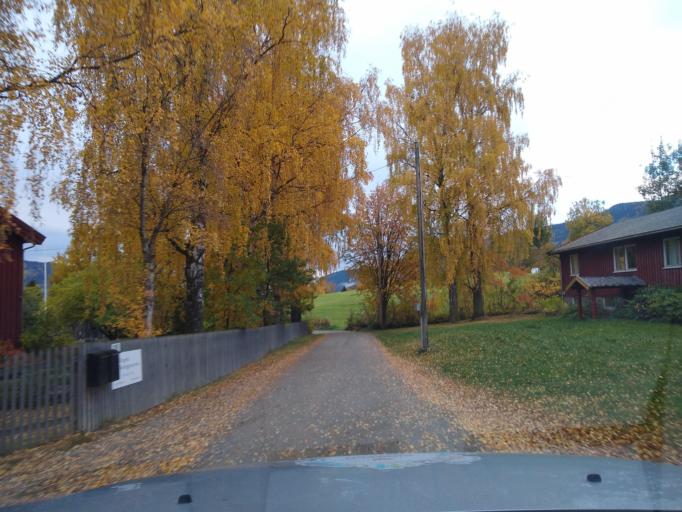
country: NO
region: Oppland
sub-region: Ringebu
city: Ringebu
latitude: 61.5421
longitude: 10.1284
